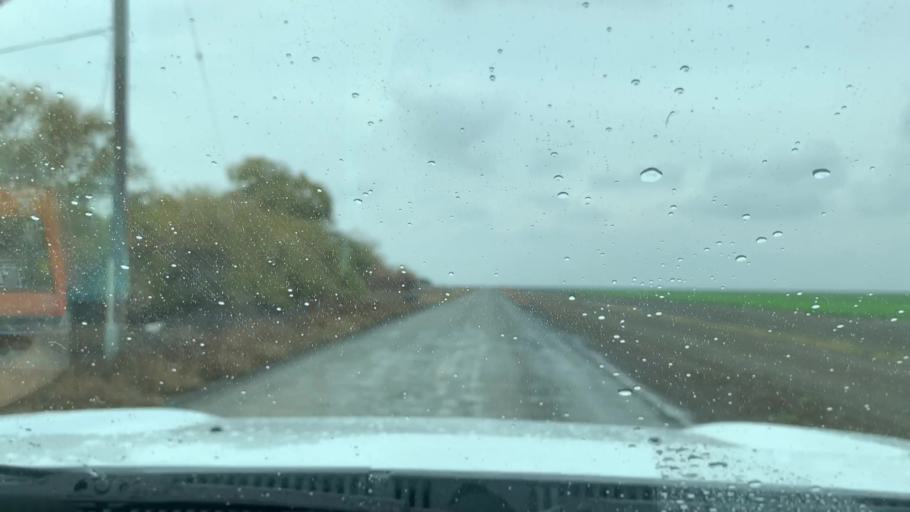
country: US
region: California
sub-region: Kings County
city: Corcoran
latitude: 36.0072
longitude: -119.5495
